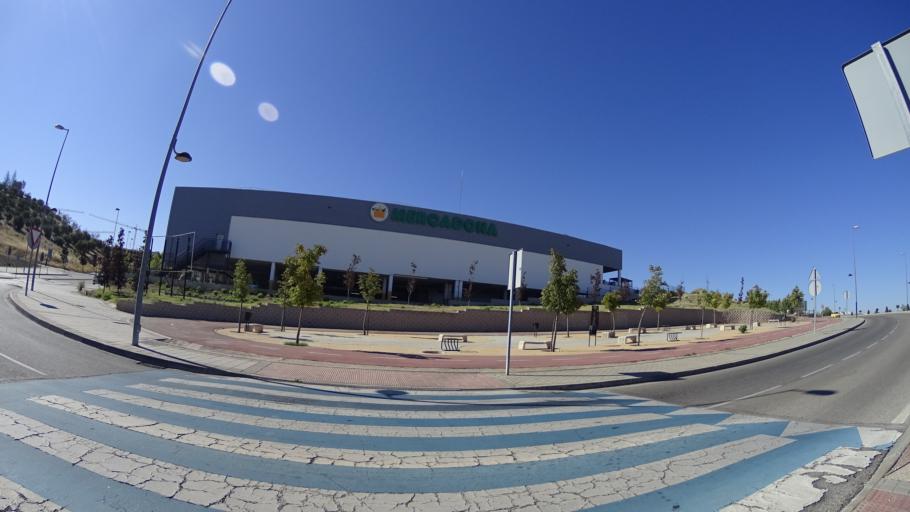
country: ES
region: Madrid
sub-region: Provincia de Madrid
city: Arganda
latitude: 40.3032
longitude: -3.4526
